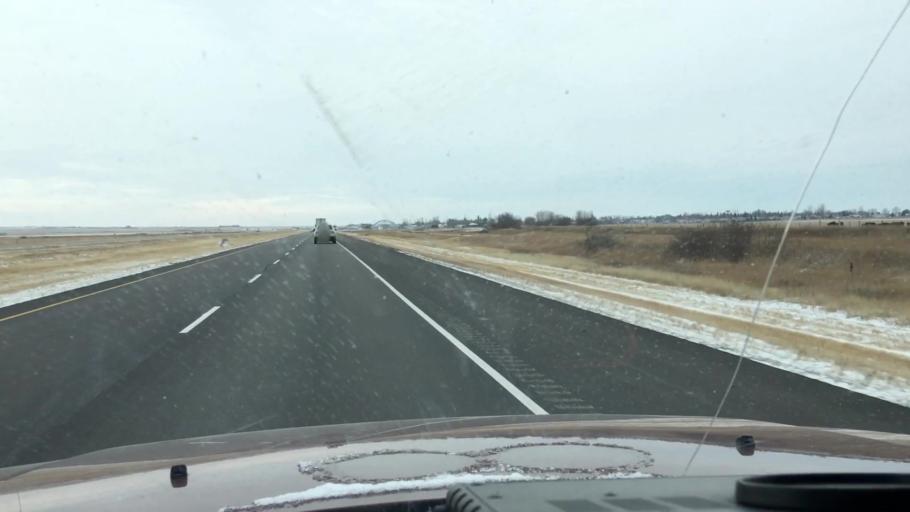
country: CA
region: Saskatchewan
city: Saskatoon
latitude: 51.8251
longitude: -106.5006
